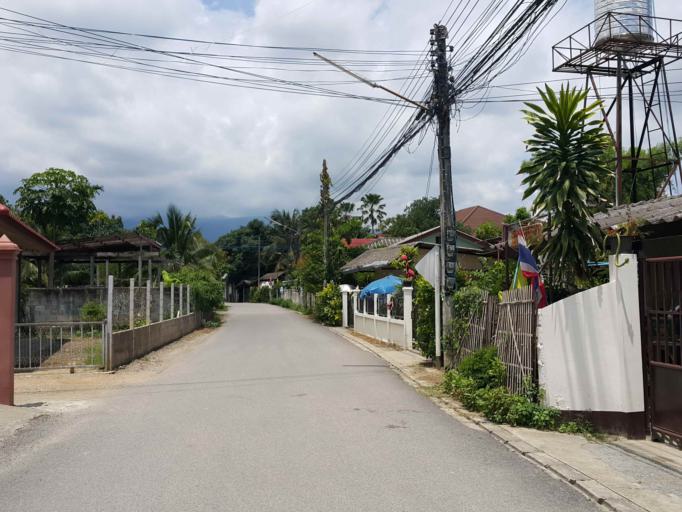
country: TH
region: Chiang Mai
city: Chiang Mai
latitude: 18.8313
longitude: 99.0026
